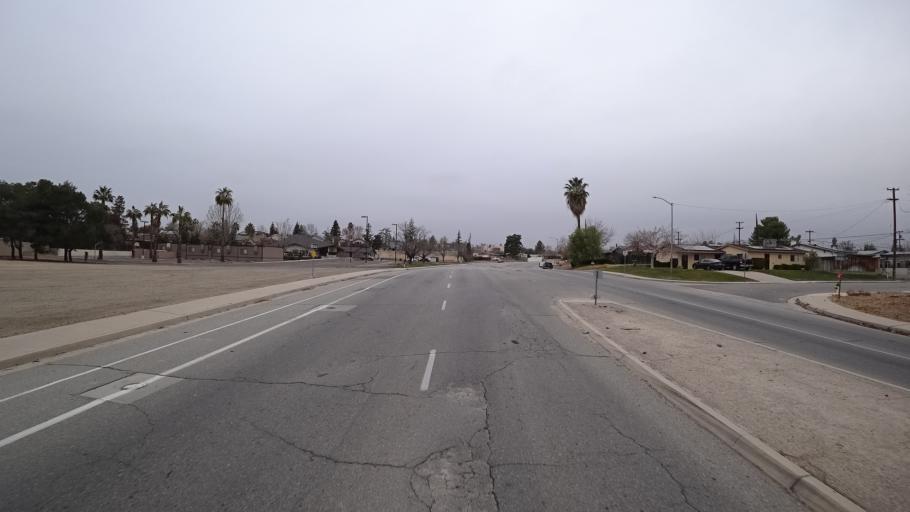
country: US
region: California
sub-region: Kern County
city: Bakersfield
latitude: 35.3799
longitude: -118.9321
